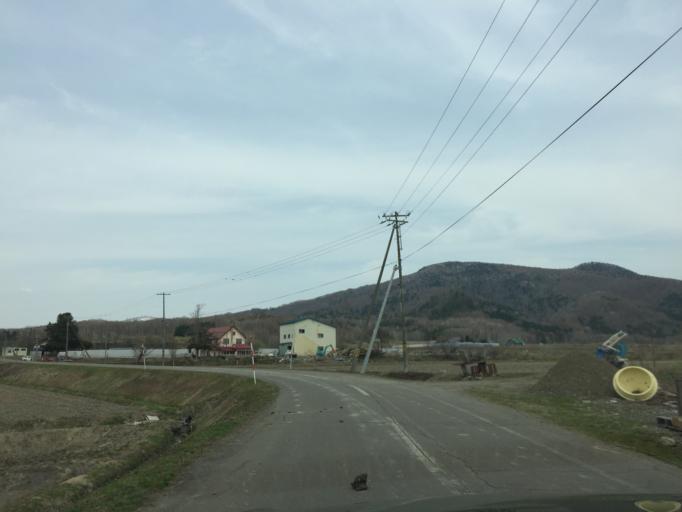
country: JP
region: Hokkaido
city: Ashibetsu
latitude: 43.6158
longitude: 142.2155
